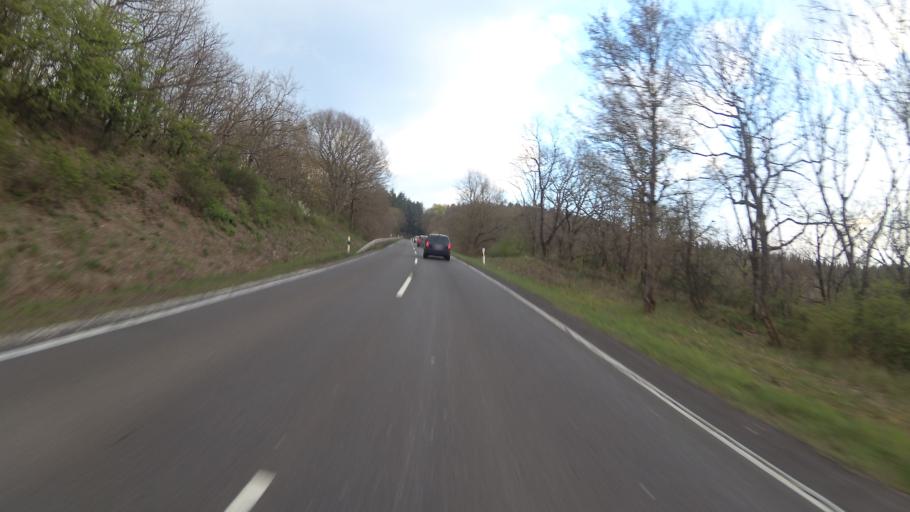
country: DE
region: Rheinland-Pfalz
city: Veldenz
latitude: 49.8954
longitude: 7.0375
